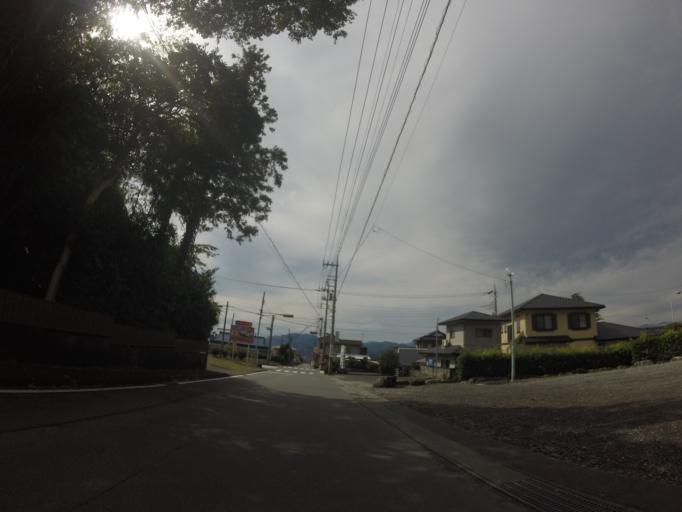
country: JP
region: Shizuoka
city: Fuji
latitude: 35.2116
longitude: 138.6768
